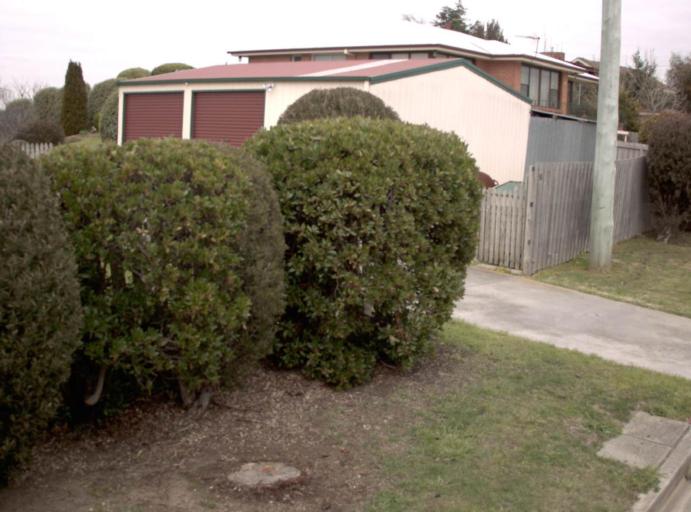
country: AU
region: Tasmania
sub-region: Launceston
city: Newstead
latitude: -41.4485
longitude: 147.1780
